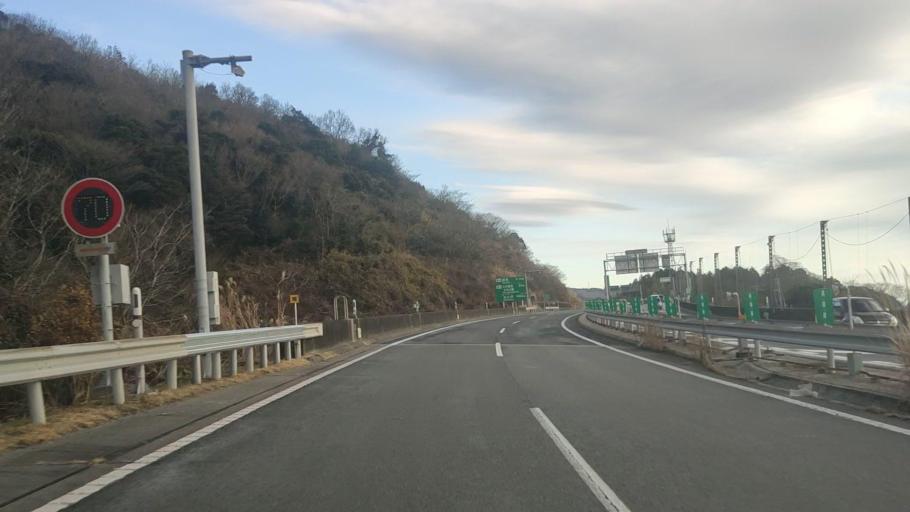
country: JP
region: Oita
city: Hiji
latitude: 33.3566
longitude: 131.4468
